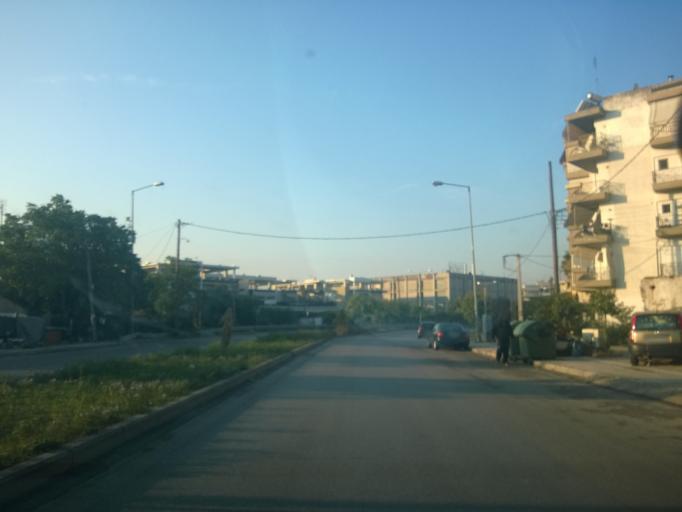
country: GR
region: Central Macedonia
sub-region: Nomos Thessalonikis
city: Ampelokipoi
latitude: 40.6631
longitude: 22.9282
